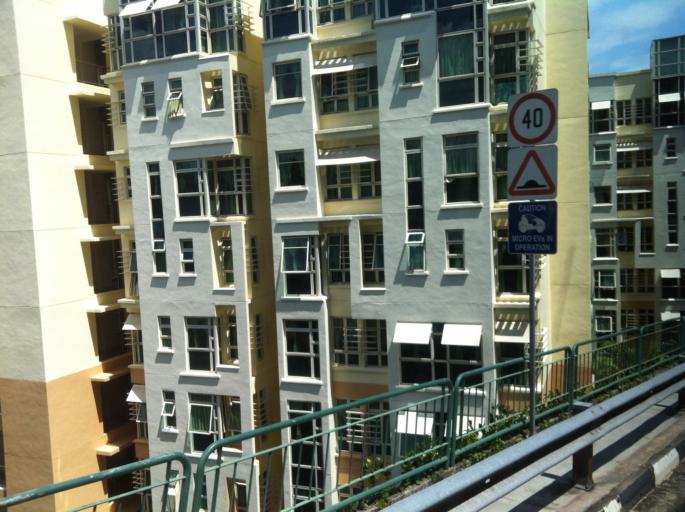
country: SG
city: Singapore
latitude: 1.2916
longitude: 103.7825
